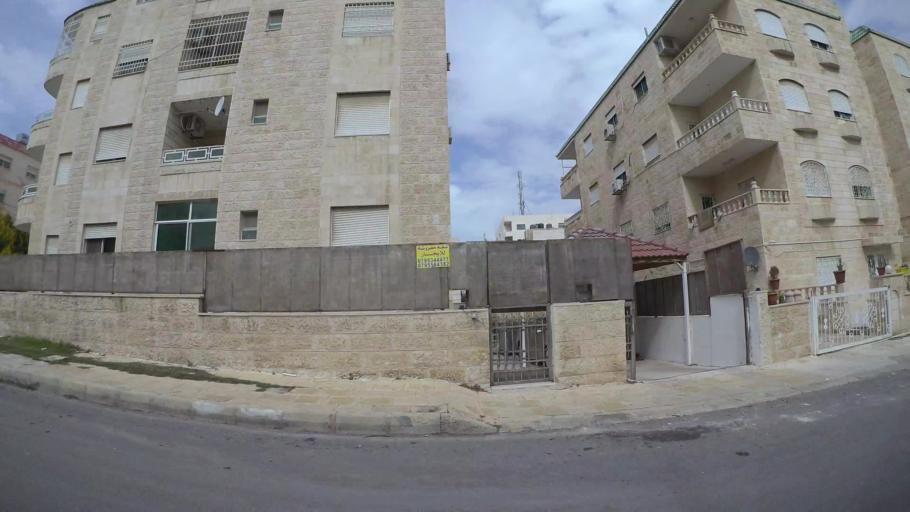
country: JO
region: Amman
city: Amman
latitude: 31.9957
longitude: 35.9400
